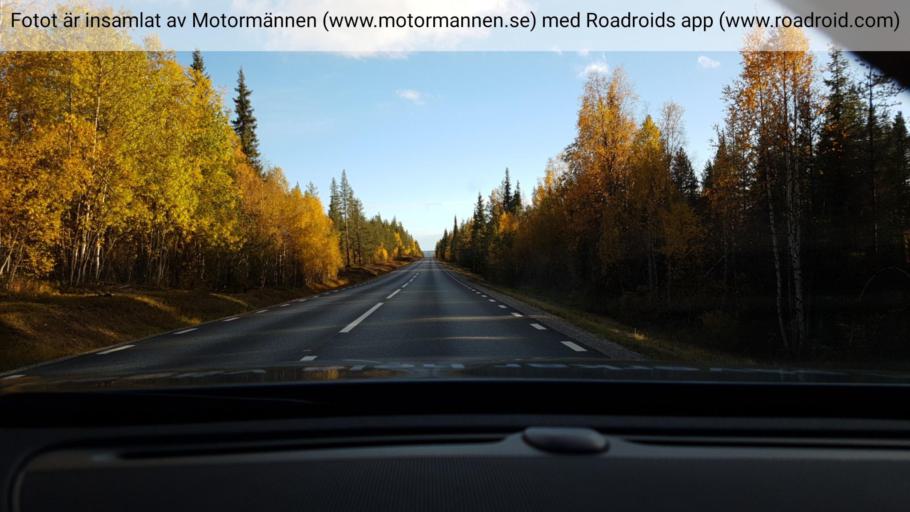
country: SE
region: Norrbotten
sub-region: Jokkmokks Kommun
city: Jokkmokk
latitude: 66.9040
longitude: 19.8269
